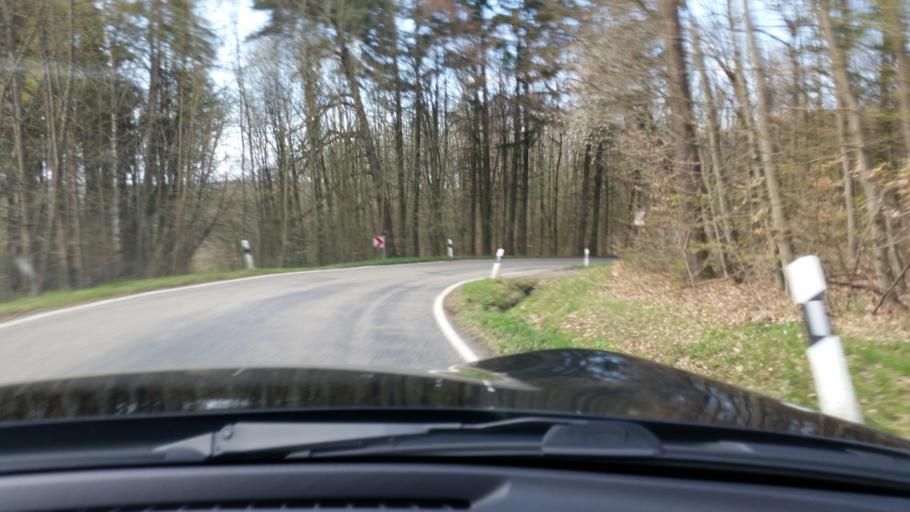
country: DE
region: Baden-Wuerttemberg
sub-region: Regierungsbezirk Stuttgart
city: Widdern
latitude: 49.3523
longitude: 9.4076
